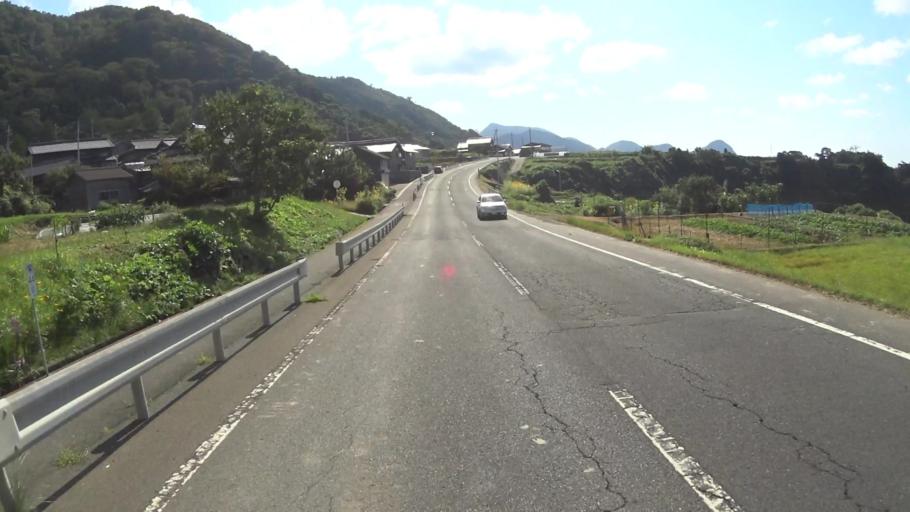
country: JP
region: Kyoto
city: Miyazu
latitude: 35.7634
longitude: 135.1917
